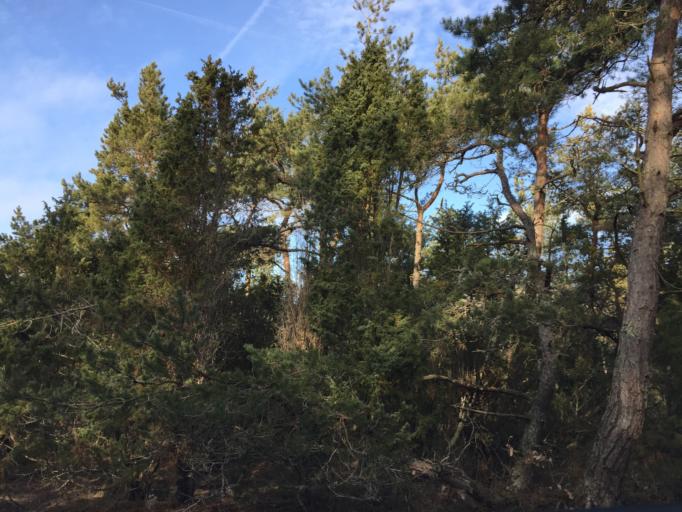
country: EE
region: Saare
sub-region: Kuressaare linn
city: Kuressaare
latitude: 58.3776
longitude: 21.9974
